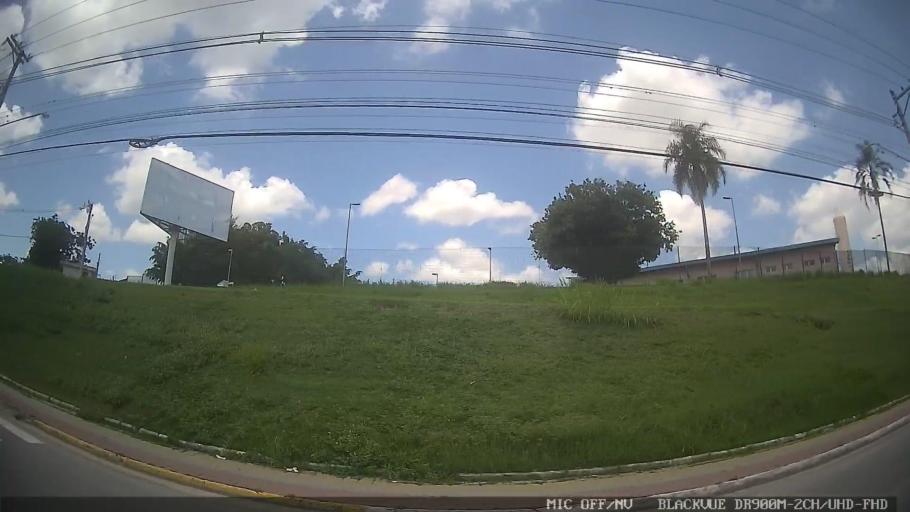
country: BR
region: Sao Paulo
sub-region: Jacarei
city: Jacarei
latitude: -23.3108
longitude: -45.9983
